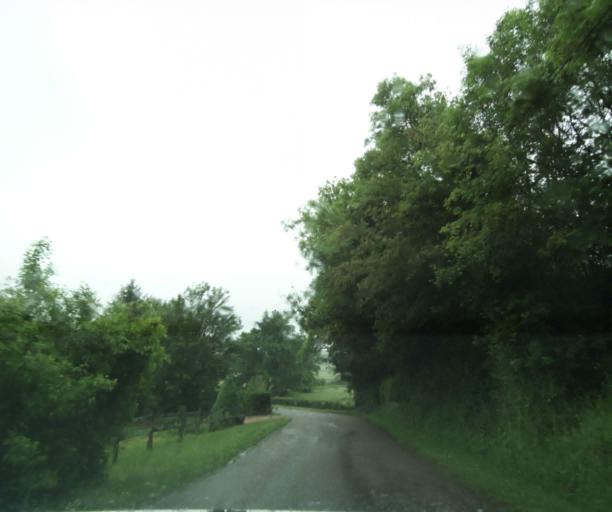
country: FR
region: Bourgogne
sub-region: Departement de Saone-et-Loire
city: Charolles
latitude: 46.3923
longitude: 4.3493
